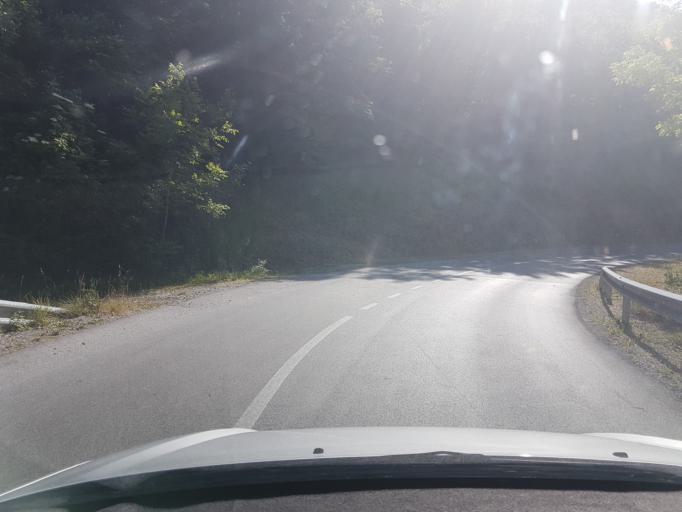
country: SI
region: Divaca
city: Divaca
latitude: 45.7559
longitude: 13.9372
